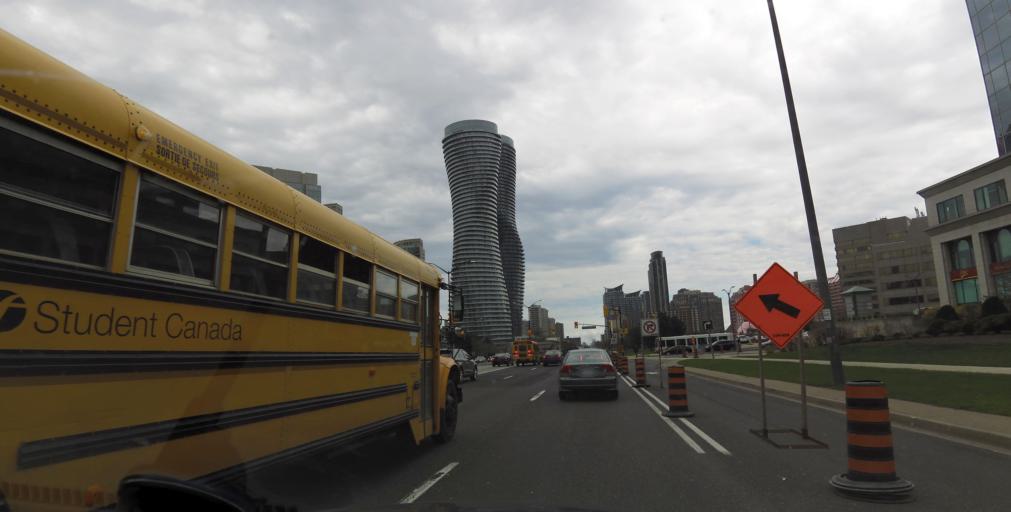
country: CA
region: Ontario
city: Mississauga
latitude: 43.5966
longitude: -79.6393
